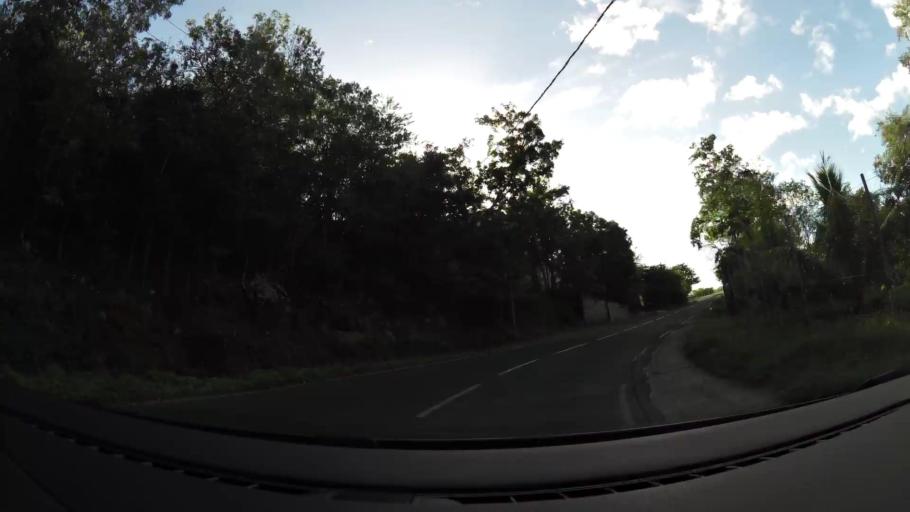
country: GP
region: Guadeloupe
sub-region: Guadeloupe
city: Pointe-Noire
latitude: 16.2585
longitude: -61.8046
